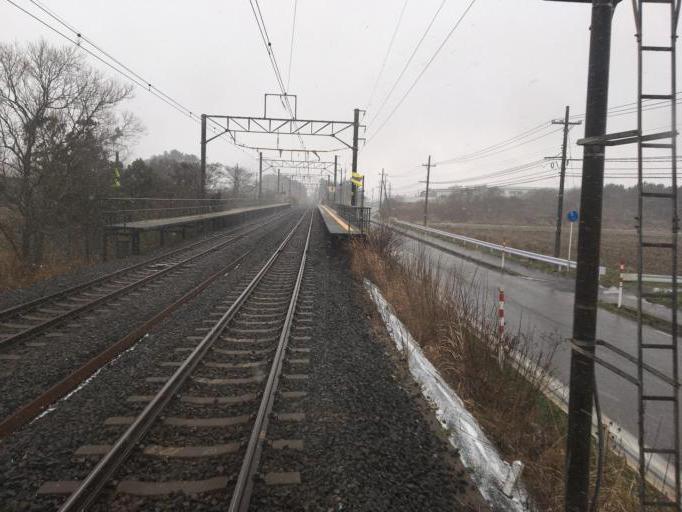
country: JP
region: Aomori
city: Aomori Shi
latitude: 40.9890
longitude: 140.6520
